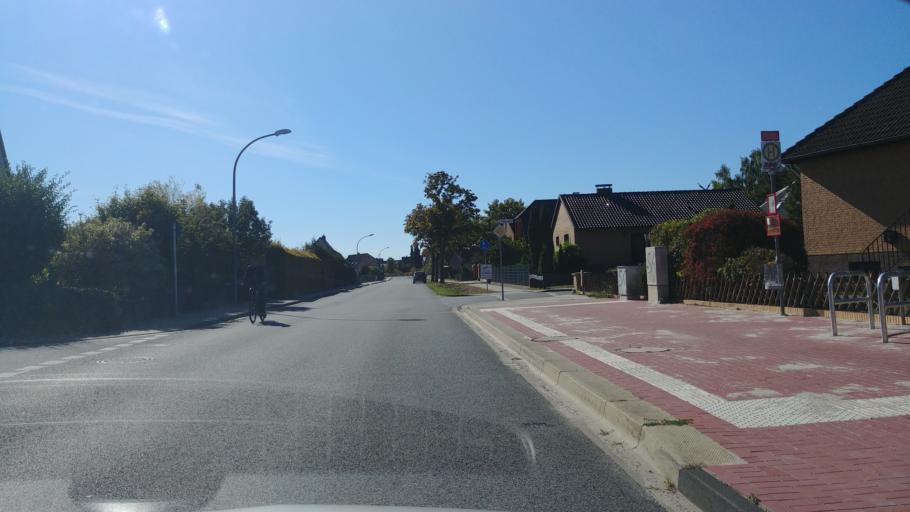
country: DE
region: Lower Saxony
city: Meinersen
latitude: 52.4771
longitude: 10.3625
